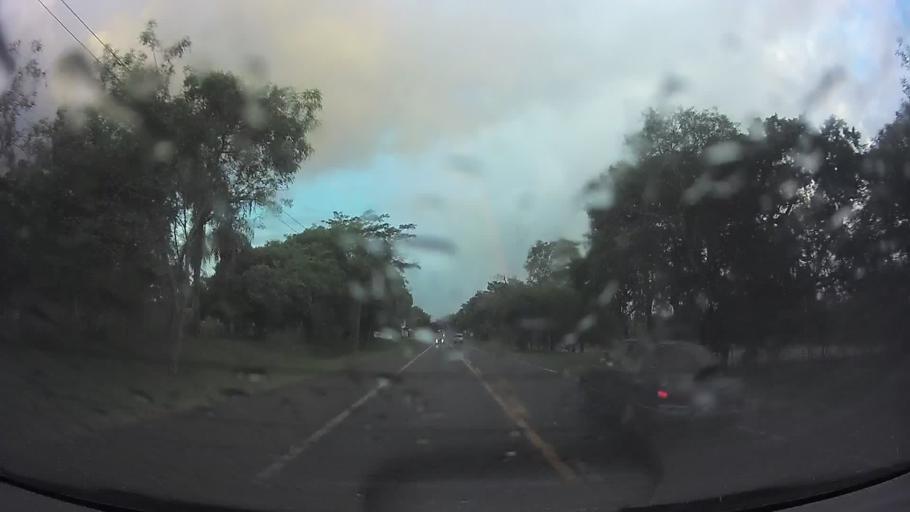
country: PY
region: Paraguari
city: Yaguaron
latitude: -25.5747
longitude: -57.2713
